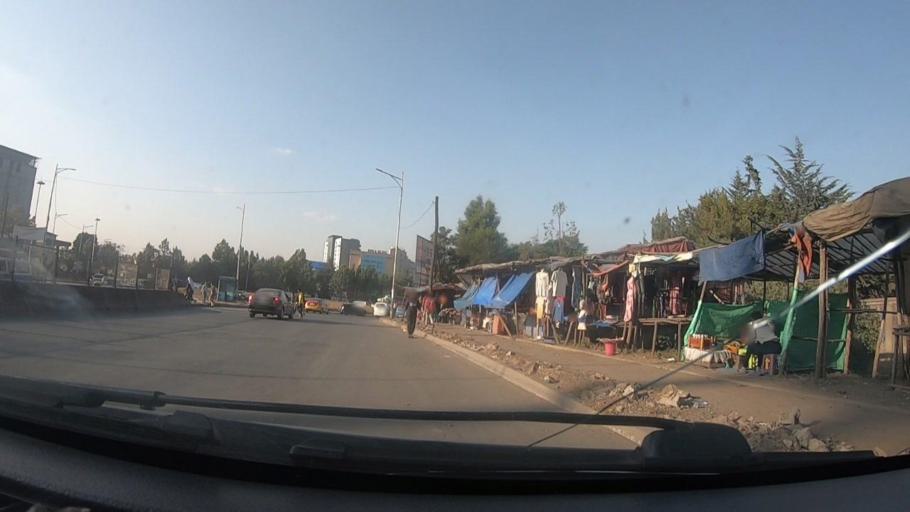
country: ET
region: Adis Abeba
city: Addis Ababa
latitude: 8.9637
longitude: 38.7331
